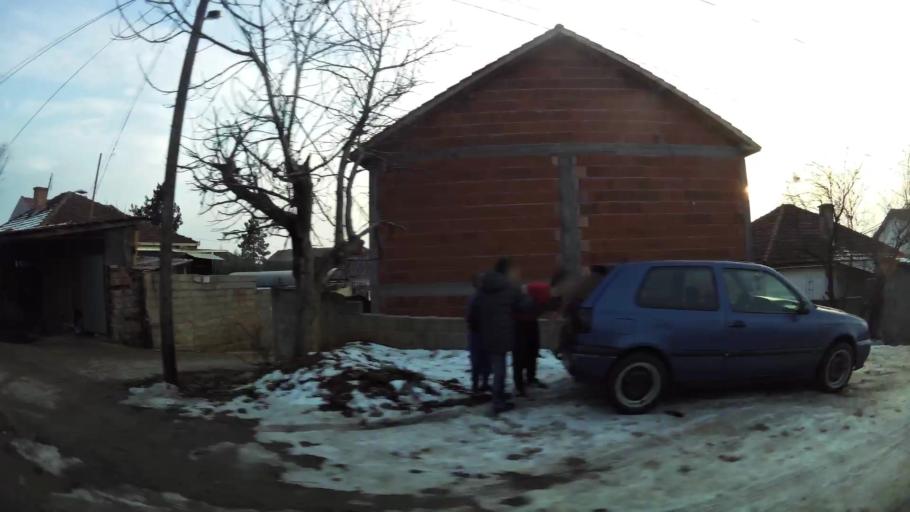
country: MK
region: Aracinovo
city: Arachinovo
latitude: 42.0268
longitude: 21.5572
